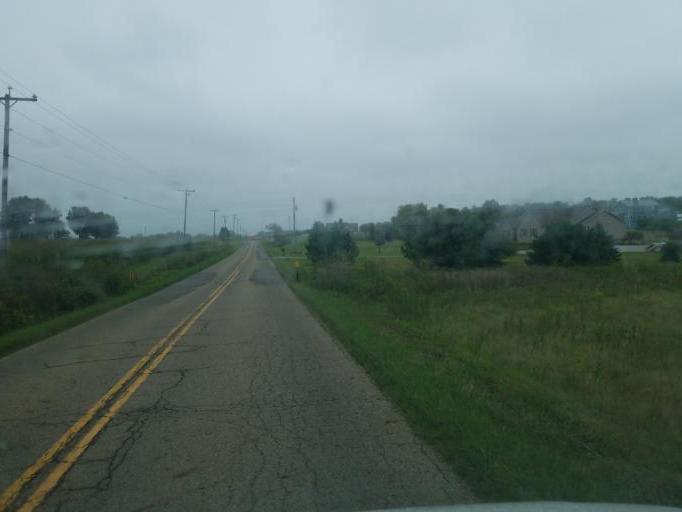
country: US
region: Ohio
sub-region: Knox County
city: Centerburg
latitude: 40.2765
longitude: -82.6904
